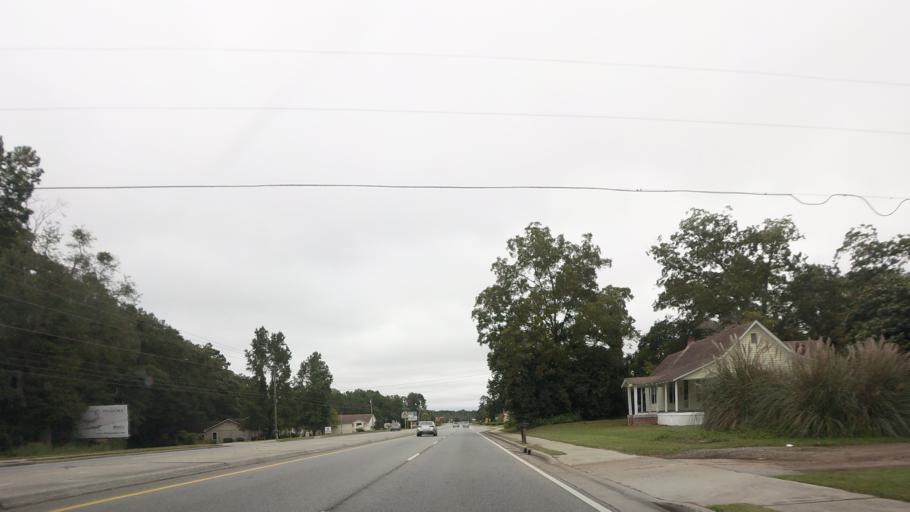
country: US
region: Georgia
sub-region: Lowndes County
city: Valdosta
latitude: 30.9043
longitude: -83.2653
